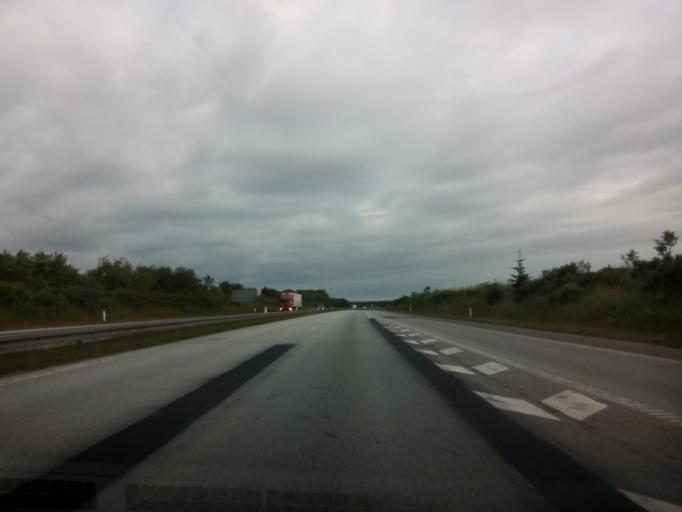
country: DK
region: North Denmark
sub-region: Hjorring Kommune
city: Vra
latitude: 57.3586
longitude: 10.0289
